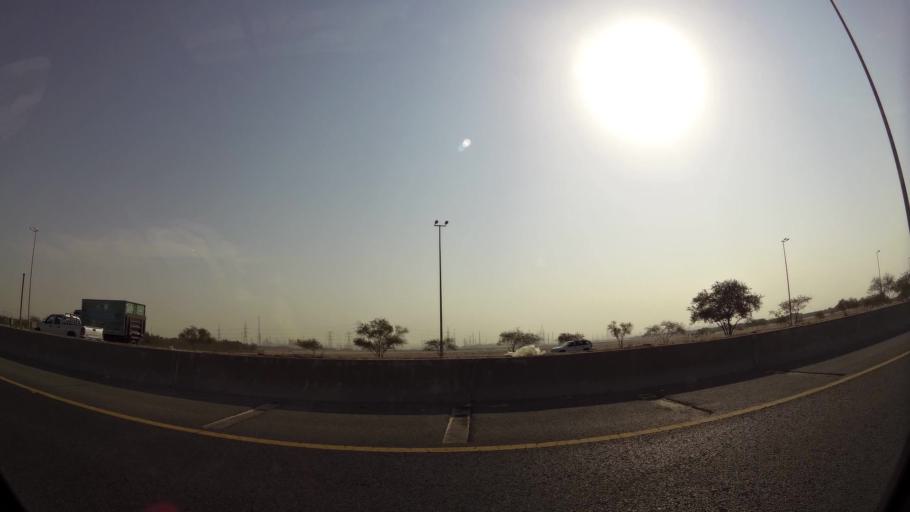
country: KW
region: Al Ahmadi
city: Al Ahmadi
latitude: 29.0559
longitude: 48.0966
